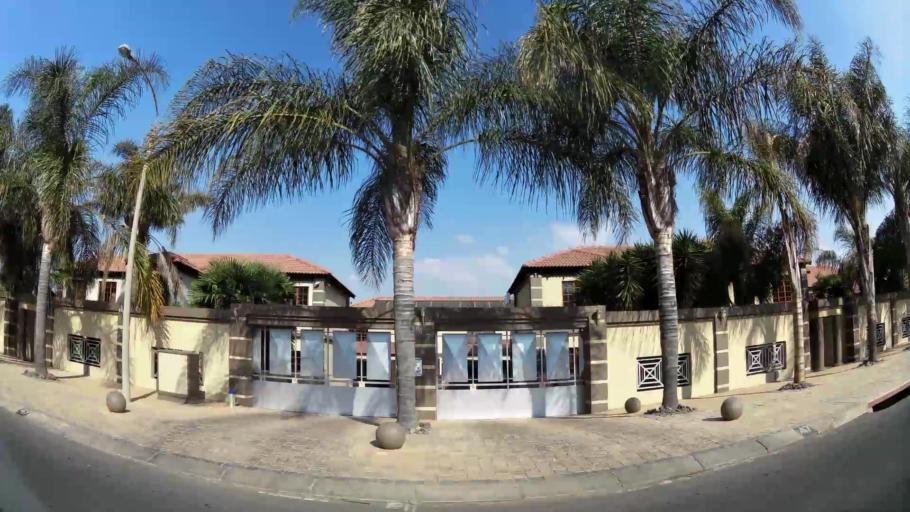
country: ZA
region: Gauteng
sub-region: Ekurhuleni Metropolitan Municipality
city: Boksburg
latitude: -26.1902
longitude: 28.2616
